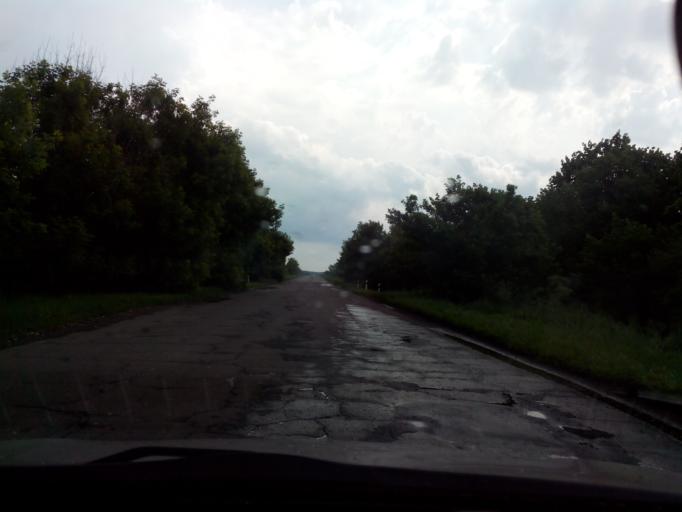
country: RU
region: Volgograd
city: Mikhaylovka
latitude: 49.9081
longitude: 42.9346
